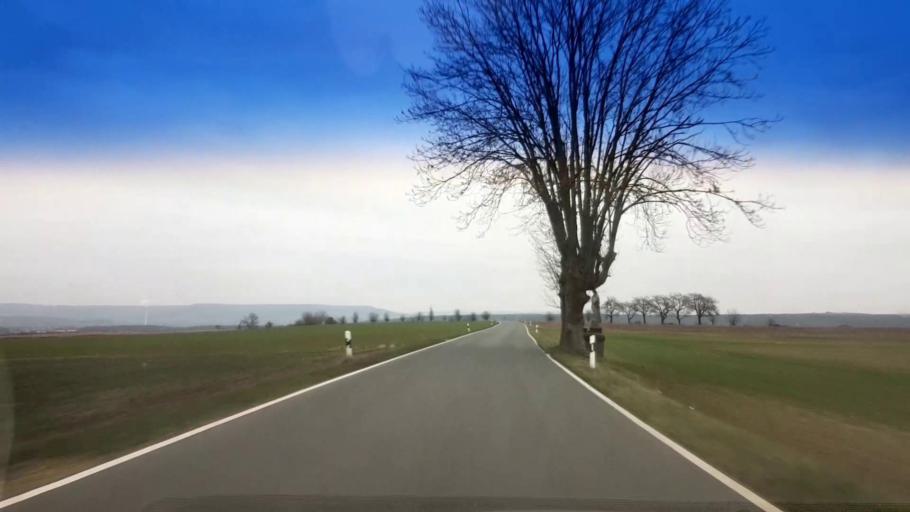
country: DE
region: Bavaria
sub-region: Upper Franconia
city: Hallerndorf
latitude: 49.7628
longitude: 10.9689
